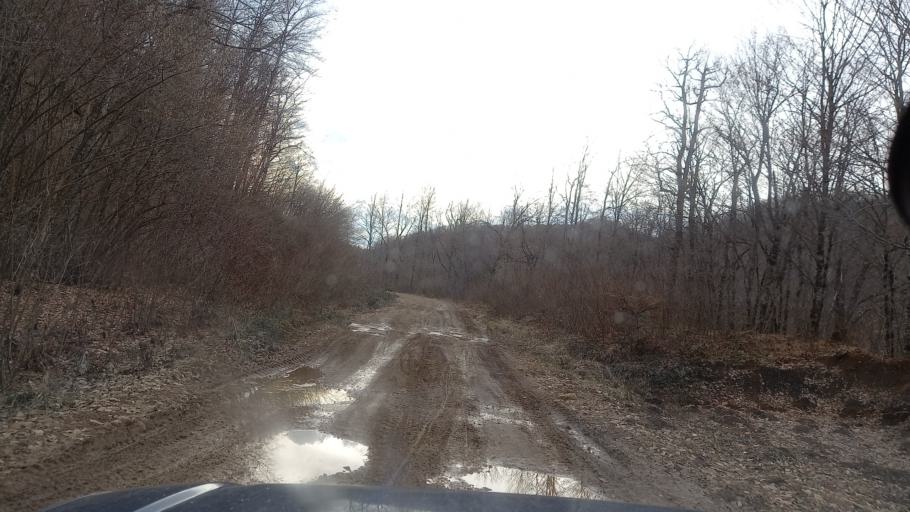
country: RU
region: Adygeya
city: Kamennomostskiy
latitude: 44.1702
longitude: 40.2983
